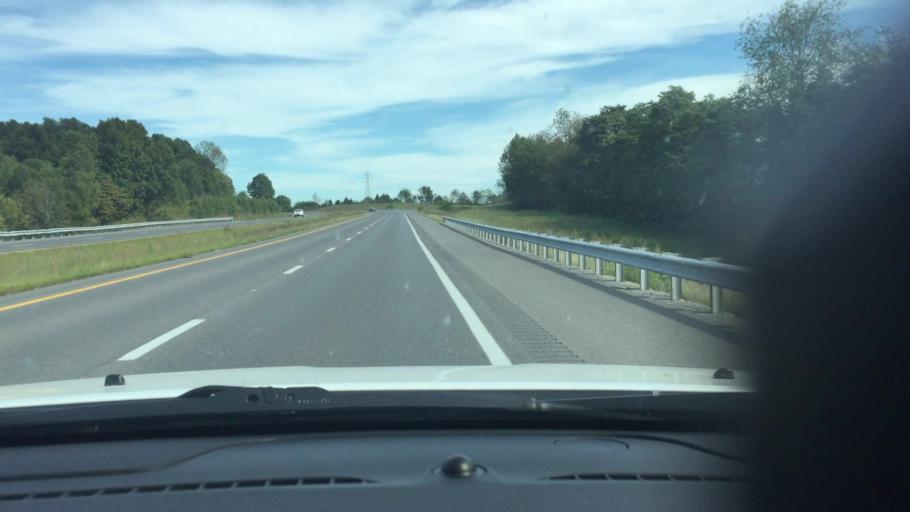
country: US
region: Kentucky
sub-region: Caldwell County
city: Princeton
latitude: 37.1100
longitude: -87.9547
